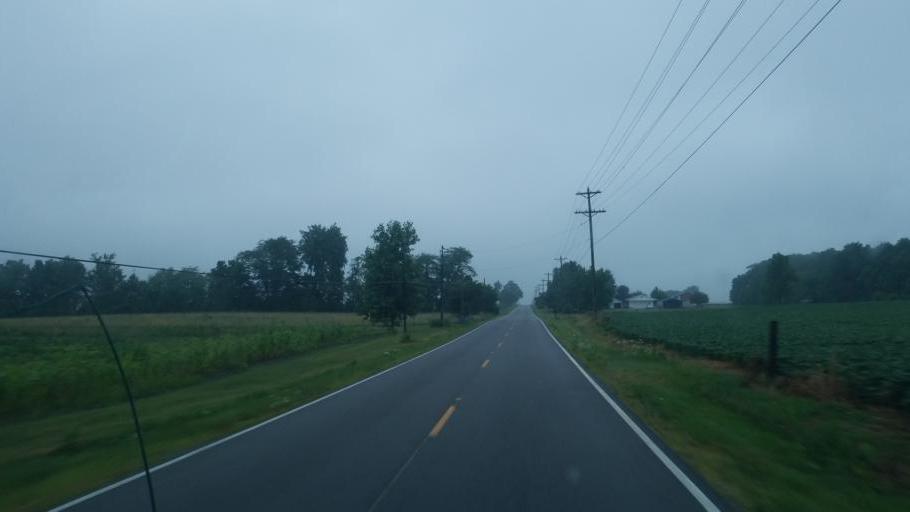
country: US
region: Ohio
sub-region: Defiance County
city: Hicksville
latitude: 41.3452
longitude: -84.7093
